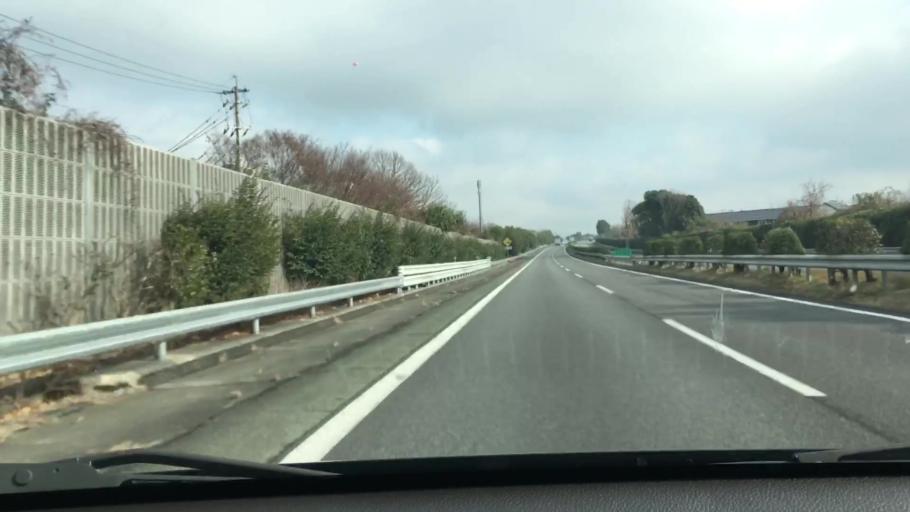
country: JP
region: Kumamoto
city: Kumamoto
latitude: 32.8573
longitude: 130.7525
